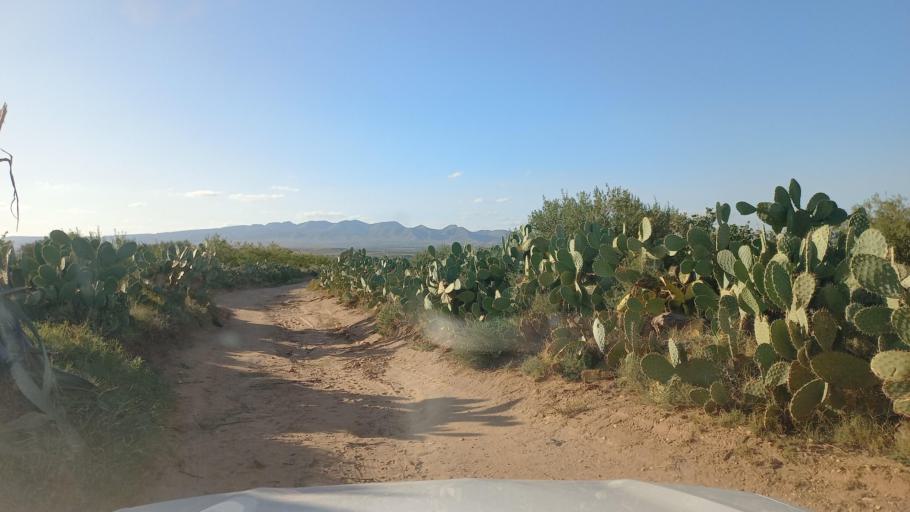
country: TN
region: Al Qasrayn
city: Sbiba
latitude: 35.3853
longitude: 9.1564
